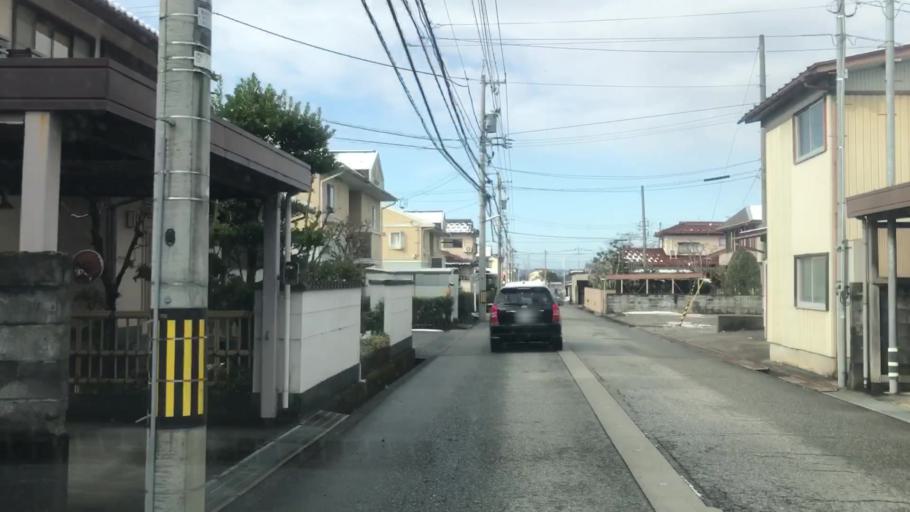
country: JP
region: Toyama
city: Toyama-shi
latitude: 36.6484
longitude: 137.2314
